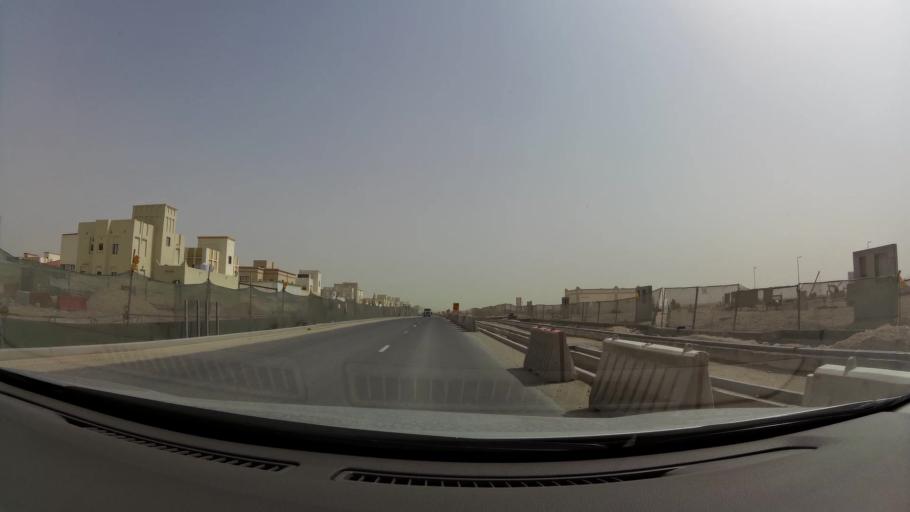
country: QA
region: Baladiyat ar Rayyan
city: Ar Rayyan
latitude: 25.2476
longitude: 51.3619
